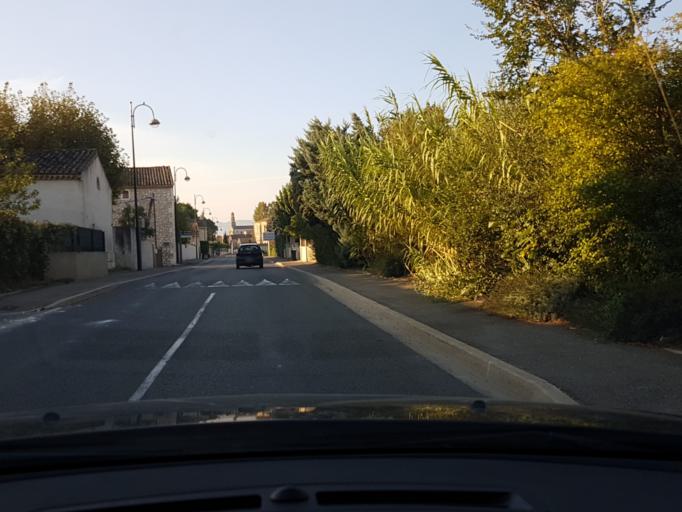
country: FR
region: Provence-Alpes-Cote d'Azur
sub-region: Departement des Bouches-du-Rhone
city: Molleges
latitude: 43.8099
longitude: 4.9490
